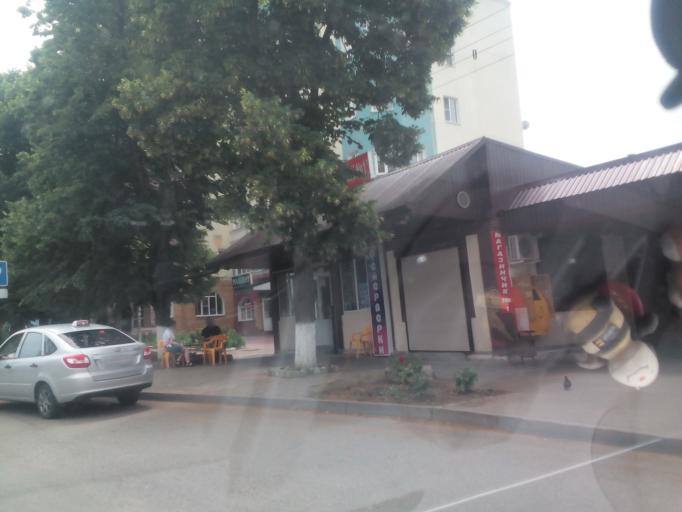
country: RU
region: Stavropol'skiy
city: Zheleznovodsk
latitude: 44.1420
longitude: 43.0070
